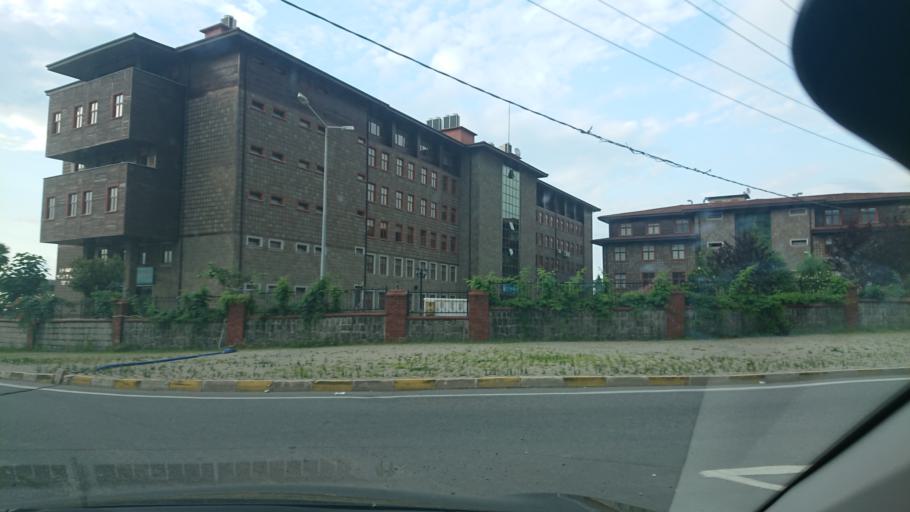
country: TR
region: Rize
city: Gundogdu
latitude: 41.0374
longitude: 40.5666
